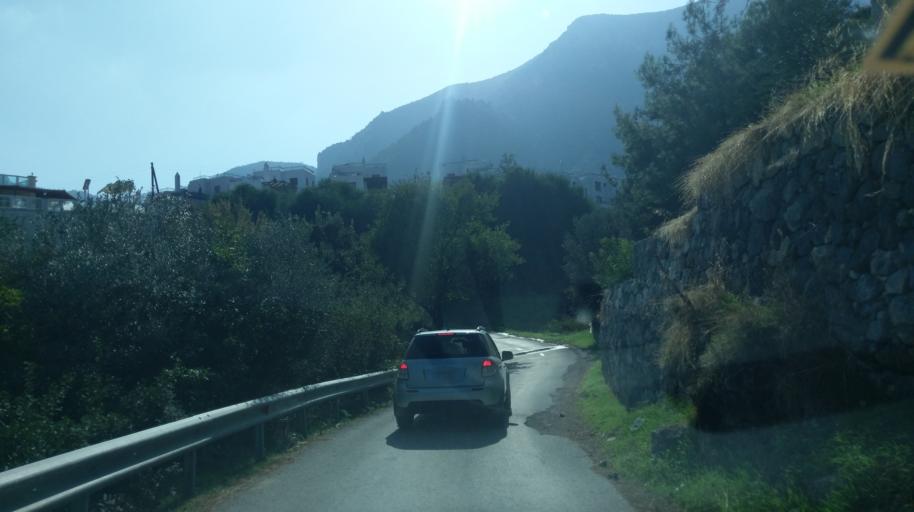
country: CY
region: Keryneia
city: Kyrenia
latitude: 35.3220
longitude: 33.2583
